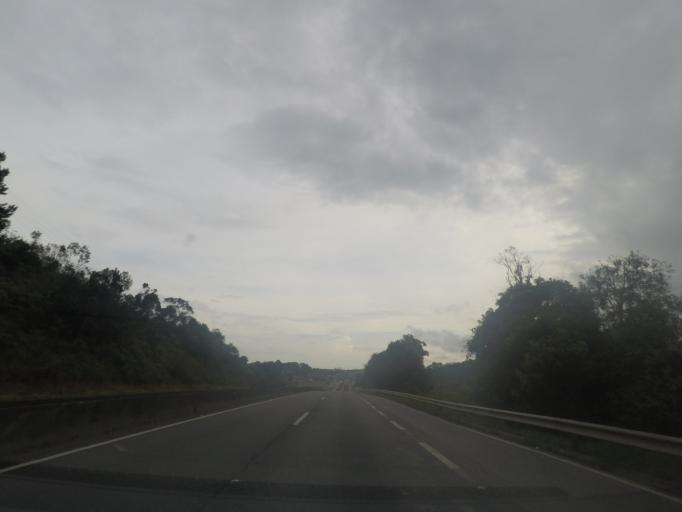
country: BR
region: Parana
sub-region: Campina Grande Do Sul
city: Campina Grande do Sul
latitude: -25.3378
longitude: -49.0370
